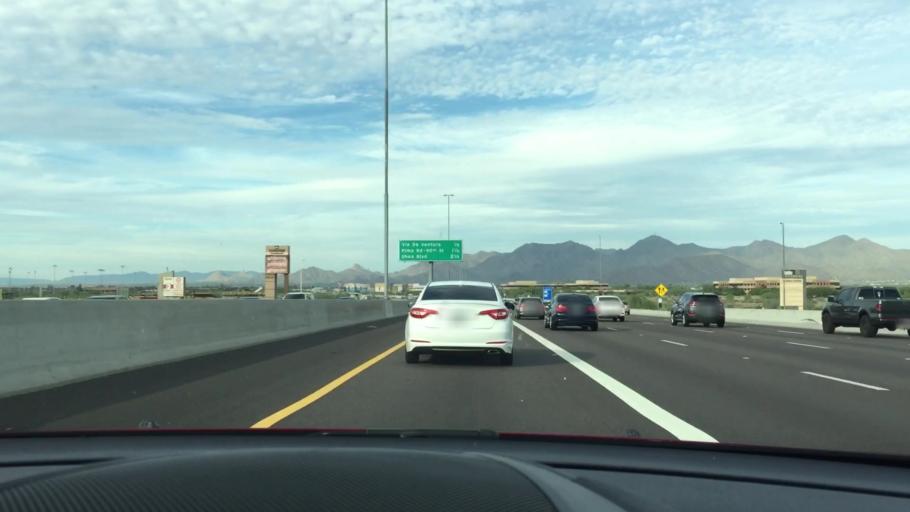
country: US
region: Arizona
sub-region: Maricopa County
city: Scottsdale
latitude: 33.5398
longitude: -111.8821
